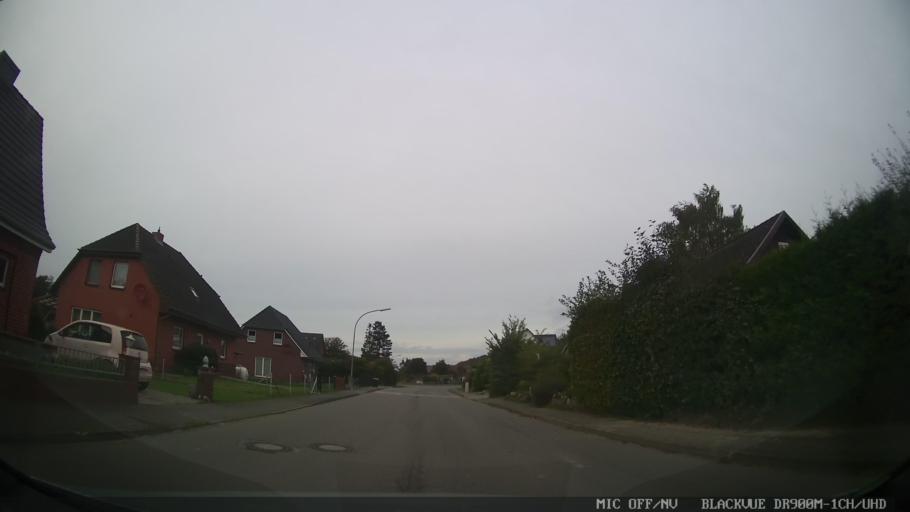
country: DE
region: Schleswig-Holstein
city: Grube
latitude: 54.2717
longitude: 11.0535
